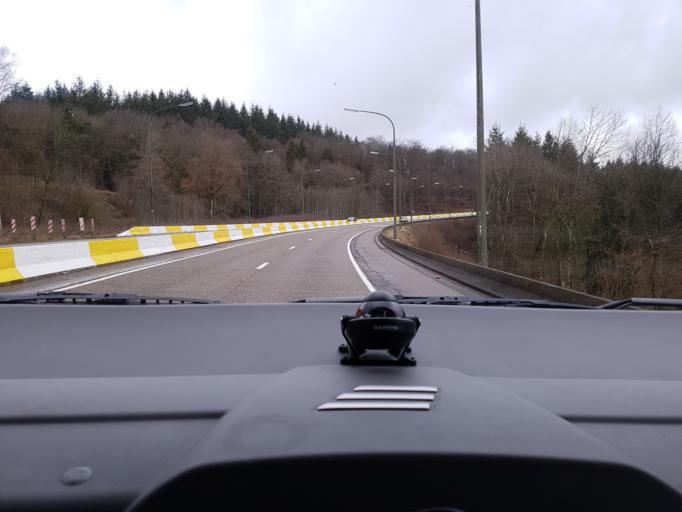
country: BE
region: Wallonia
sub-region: Province du Luxembourg
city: Tenneville
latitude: 50.0931
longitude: 5.4888
